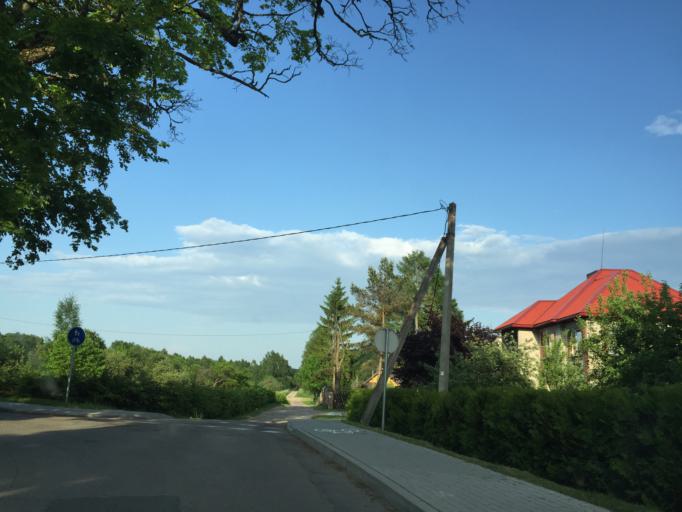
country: LT
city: Plateliai
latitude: 56.0422
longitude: 21.8206
